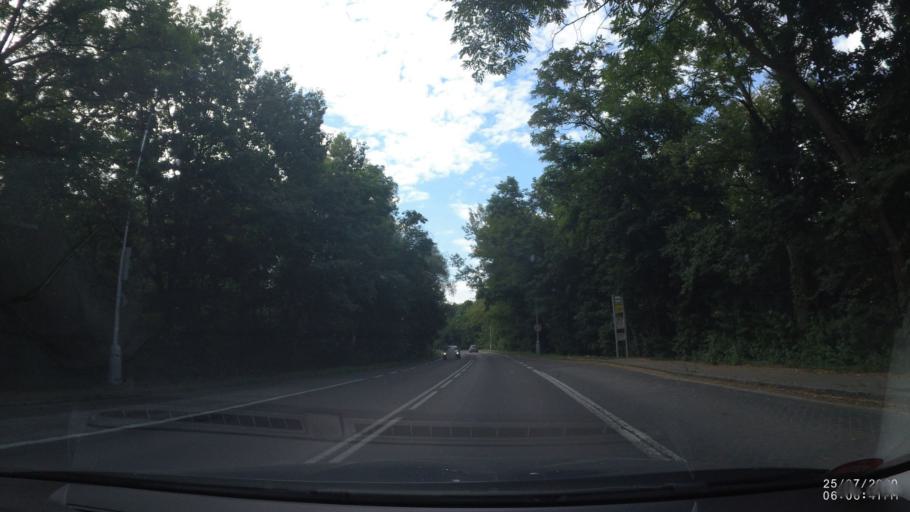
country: CZ
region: Kralovehradecky
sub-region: Okres Hradec Kralove
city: Hradec Kralove
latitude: 50.1887
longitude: 15.8313
